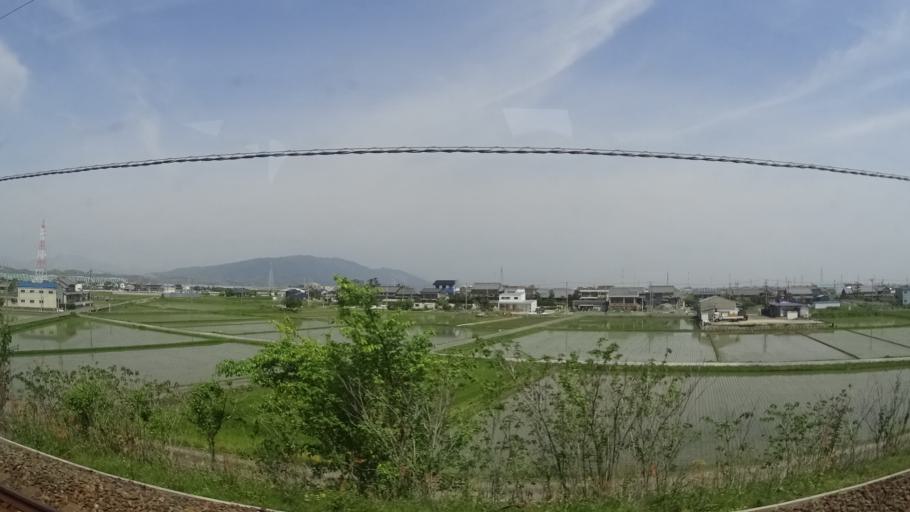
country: JP
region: Aichi
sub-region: Tsushima-shi
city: Tsushima
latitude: 35.0960
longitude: 136.6906
